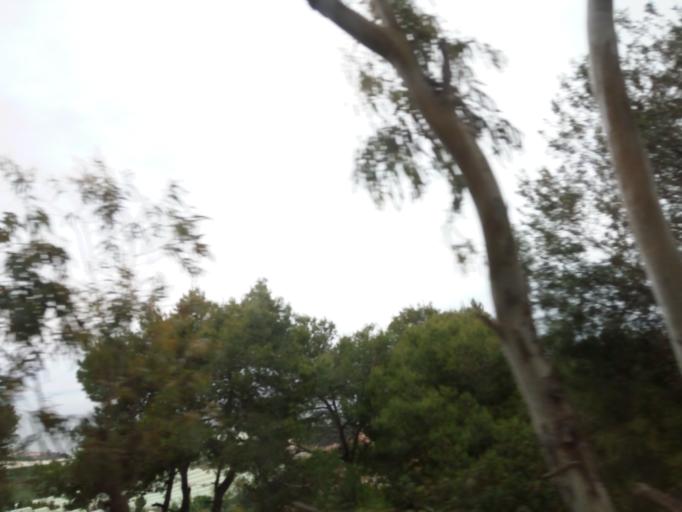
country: DZ
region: Tipaza
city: Tipasa
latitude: 36.5870
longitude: 2.5482
